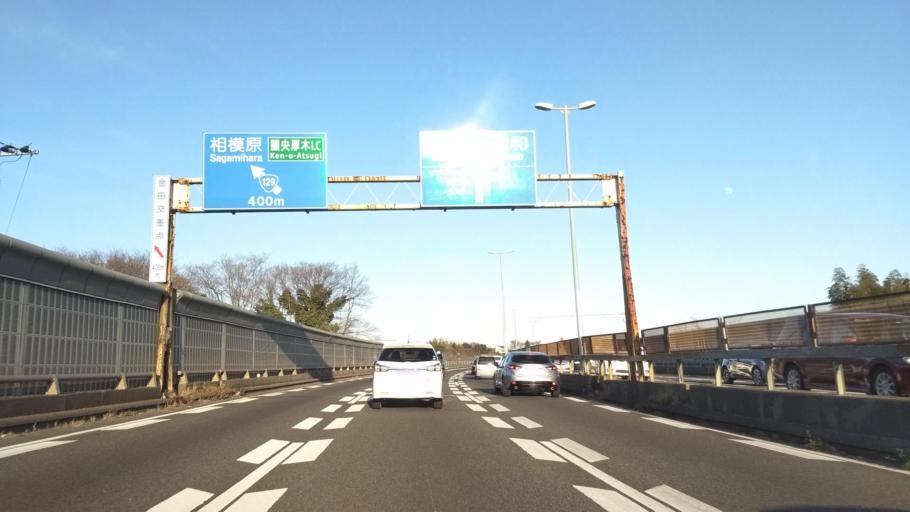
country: JP
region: Kanagawa
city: Atsugi
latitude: 35.4645
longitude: 139.3619
